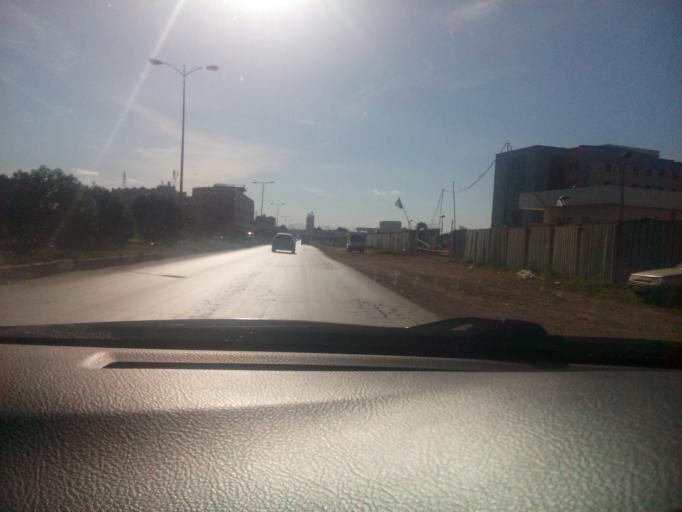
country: DZ
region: Oran
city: Sidi ech Chahmi
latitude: 35.6580
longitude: -0.5677
